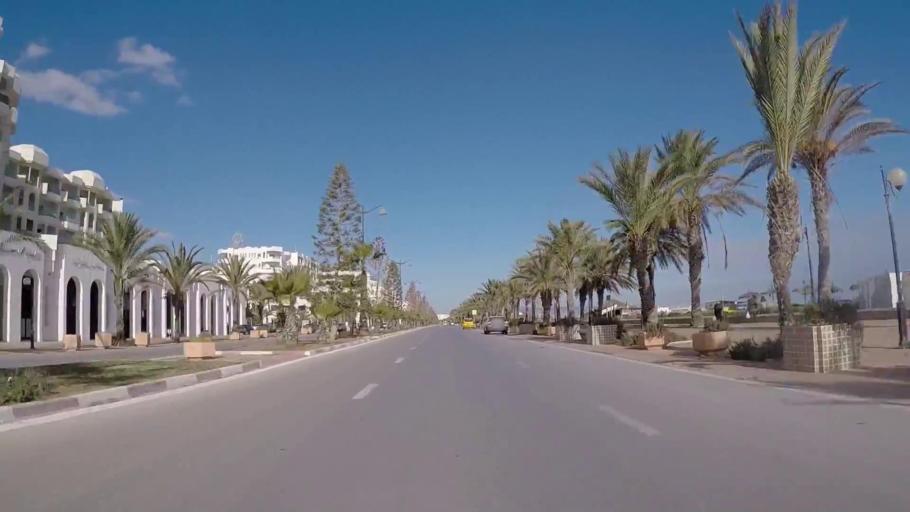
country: TN
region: Nabul
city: Al Hammamat
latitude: 36.3661
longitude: 10.5379
